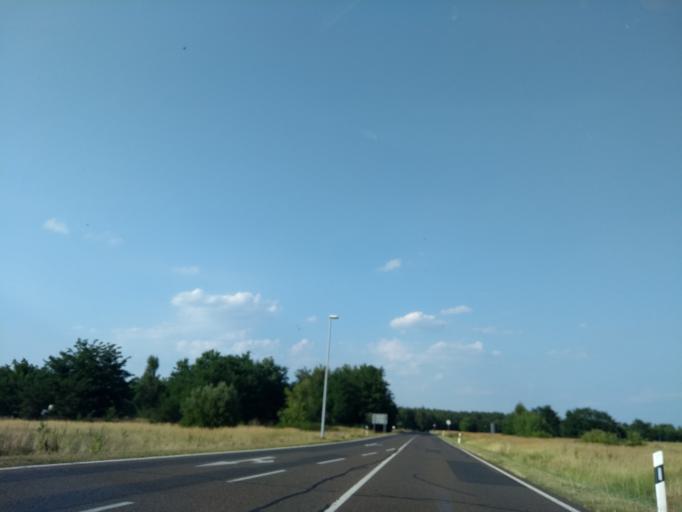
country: DE
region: Brandenburg
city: Lubbenau
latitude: 51.8328
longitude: 13.9169
